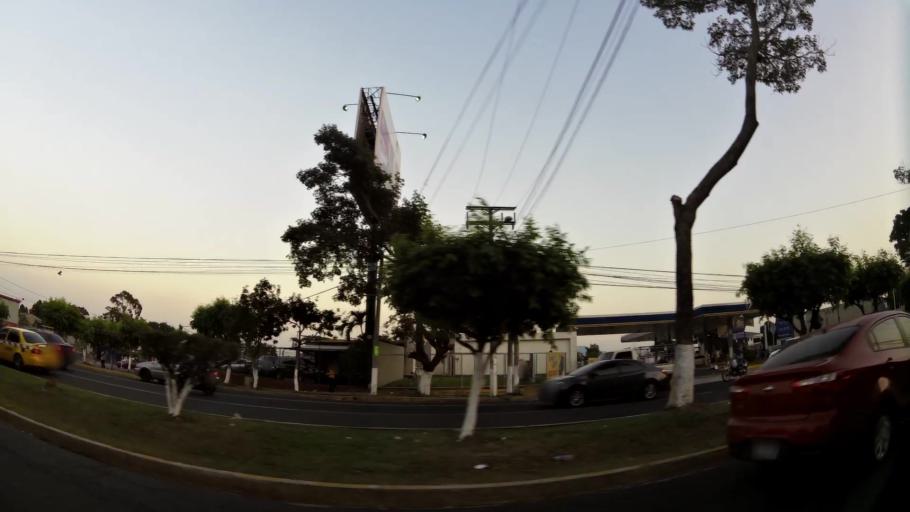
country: SV
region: San Salvador
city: Mejicanos
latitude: 13.7153
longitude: -89.2236
